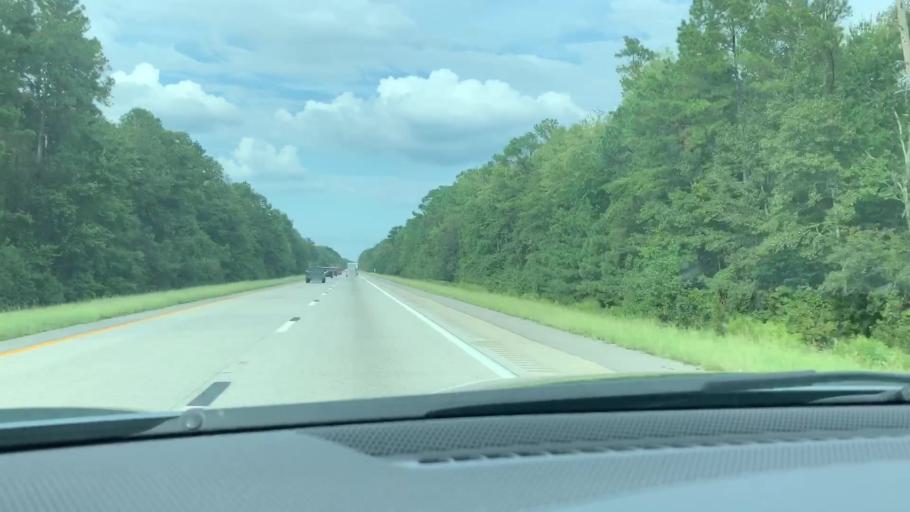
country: US
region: South Carolina
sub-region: Dorchester County
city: Saint George
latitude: 33.1047
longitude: -80.6442
